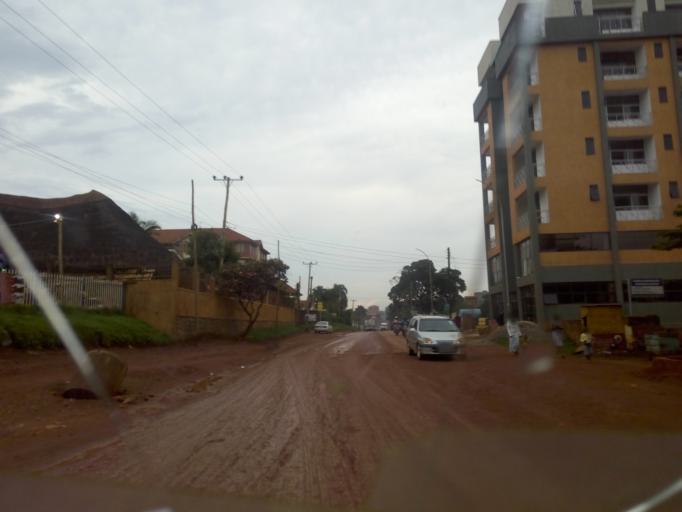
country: UG
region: Central Region
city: Kampala Central Division
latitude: 0.3240
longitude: 32.5658
